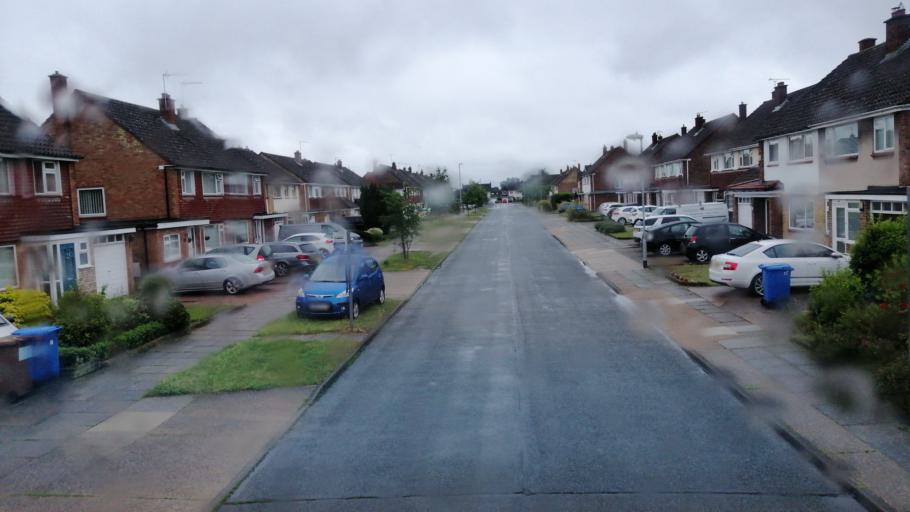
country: GB
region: England
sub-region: Suffolk
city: Kesgrave
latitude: 52.0480
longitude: 1.2050
